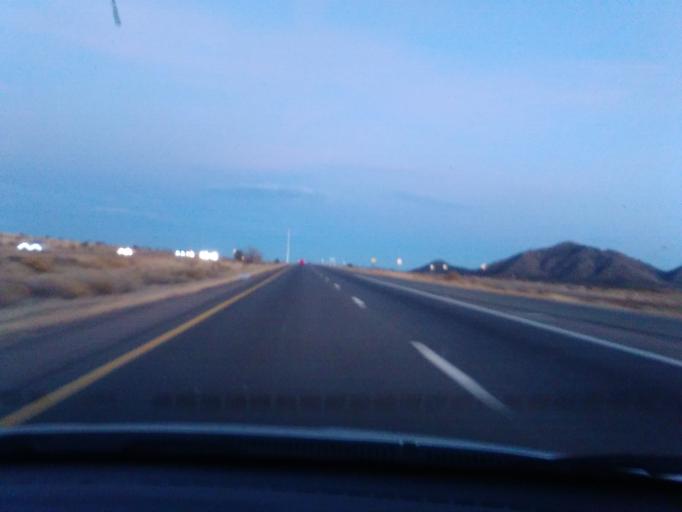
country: US
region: New Mexico
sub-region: Santa Fe County
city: La Cienega
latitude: 35.5210
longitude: -106.1772
